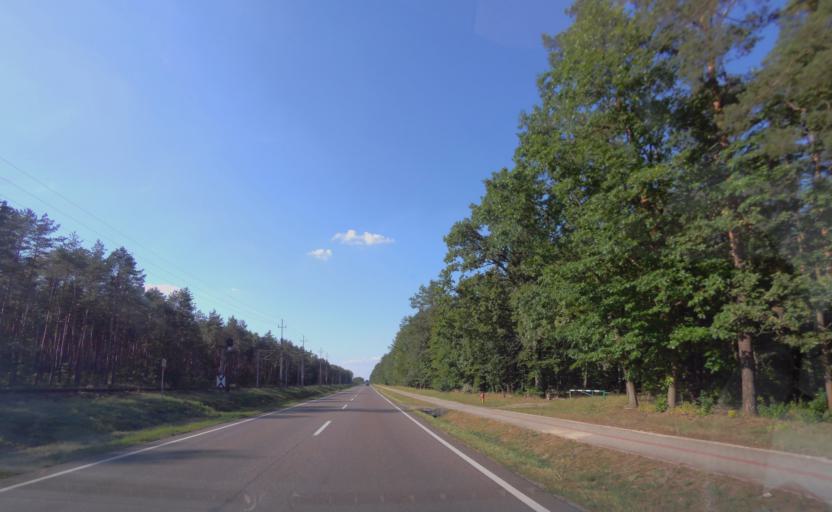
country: PL
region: Subcarpathian Voivodeship
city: Nowa Sarzyna
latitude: 50.3073
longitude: 22.3621
